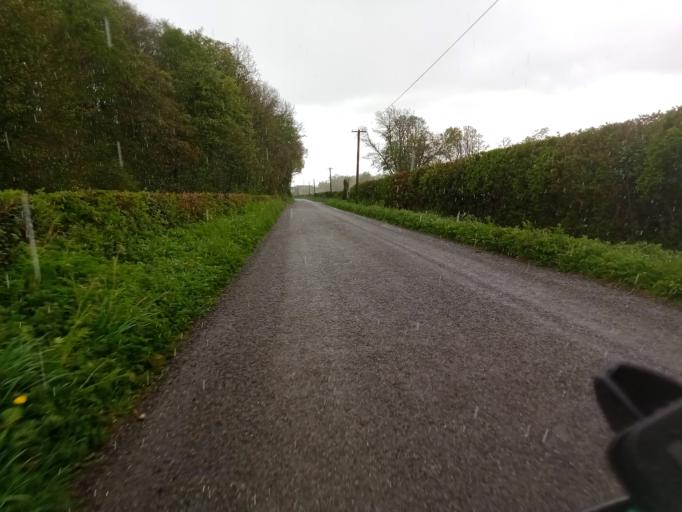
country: IE
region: Leinster
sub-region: Kilkenny
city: Kilkenny
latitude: 52.6874
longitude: -7.2696
